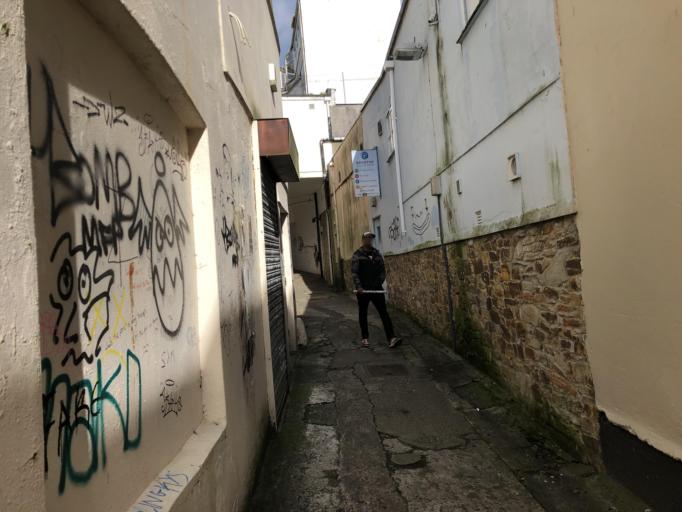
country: GB
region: England
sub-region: Cornwall
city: Truro
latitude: 50.2628
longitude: -5.0515
